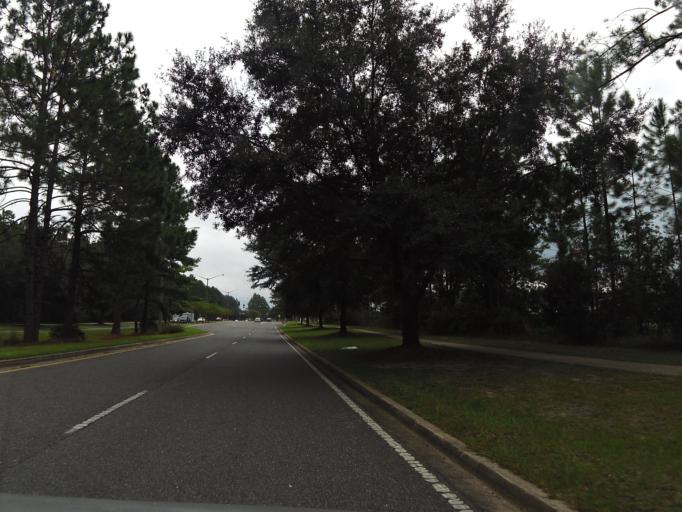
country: US
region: Florida
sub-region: Clay County
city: Lakeside
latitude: 30.1645
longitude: -81.8444
